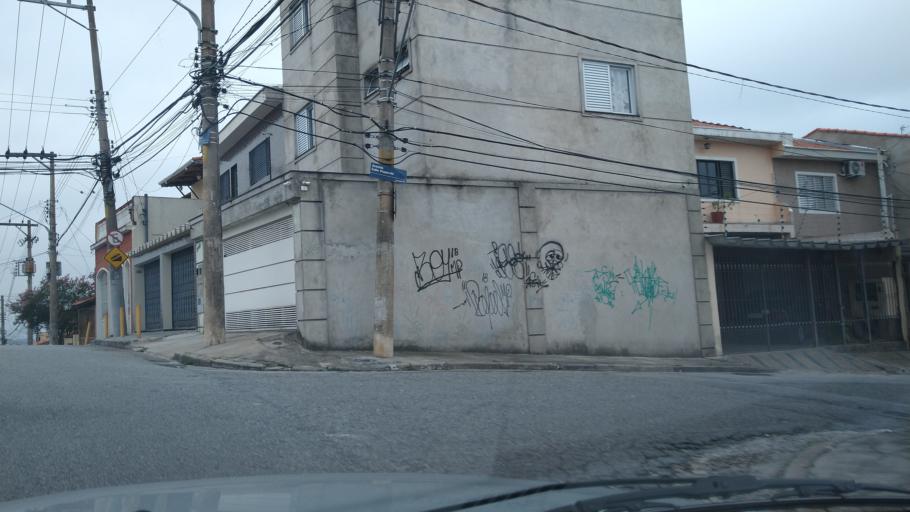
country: BR
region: Sao Paulo
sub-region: Guarulhos
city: Guarulhos
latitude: -23.4855
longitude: -46.5895
